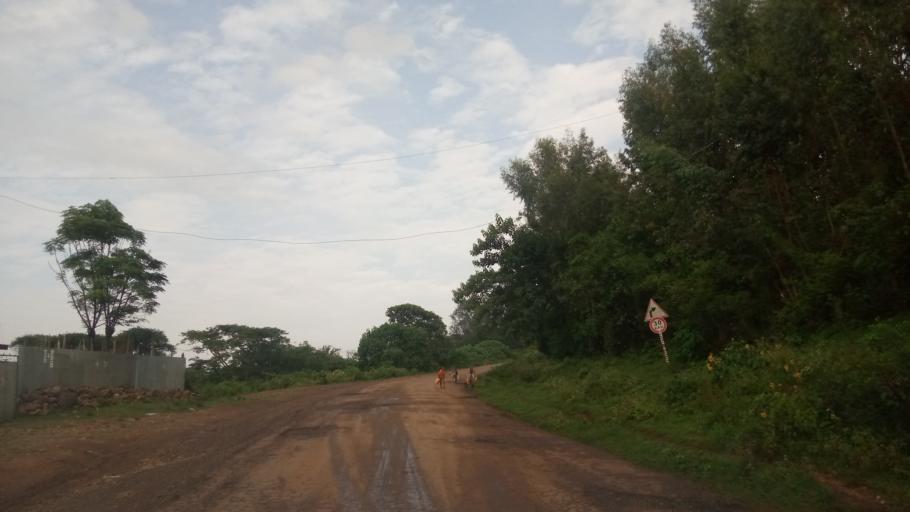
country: ET
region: Oromiya
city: Agaro
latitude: 7.8359
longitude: 36.6743
